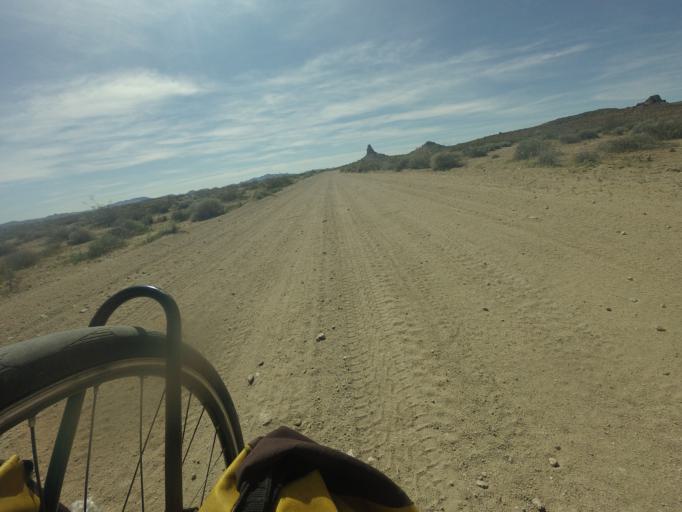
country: US
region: California
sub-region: San Bernardino County
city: Searles Valley
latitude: 35.5788
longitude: -117.4298
